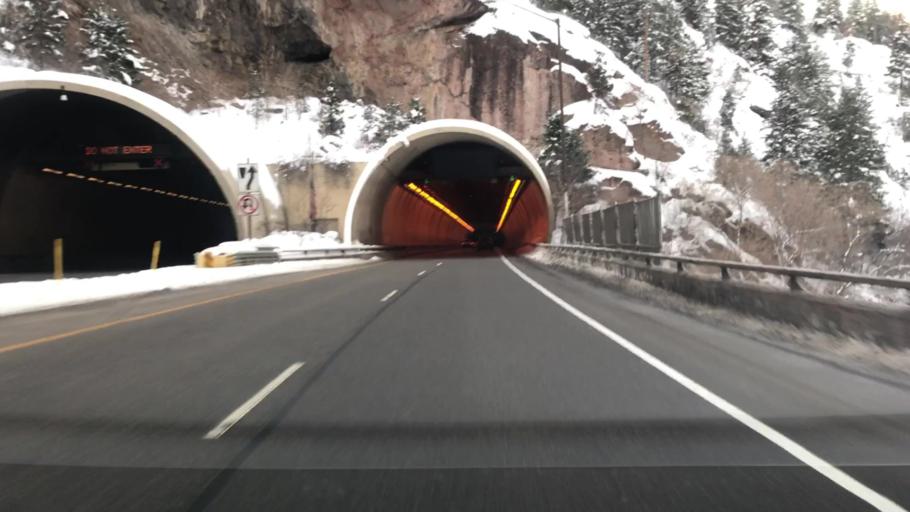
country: US
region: Colorado
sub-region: Garfield County
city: Glenwood Springs
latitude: 39.5910
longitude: -107.1812
